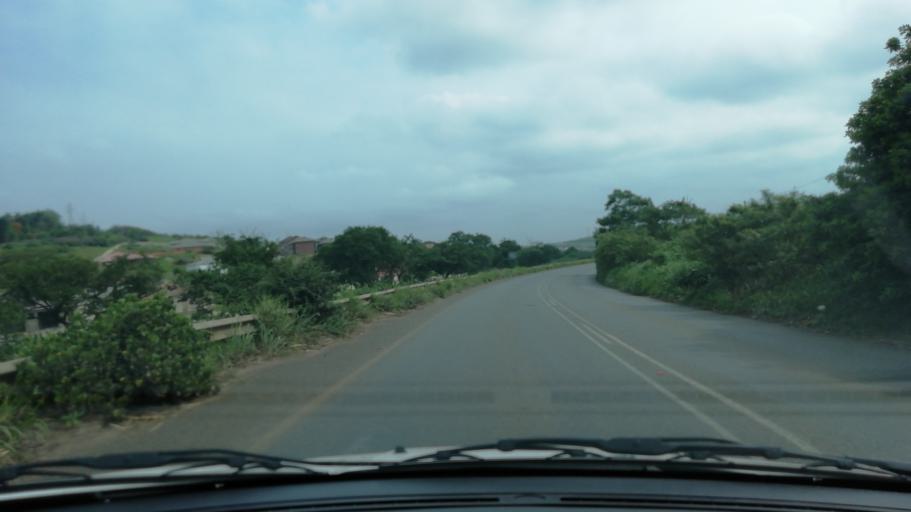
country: ZA
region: KwaZulu-Natal
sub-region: uThungulu District Municipality
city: Empangeni
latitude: -28.7478
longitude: 31.8805
